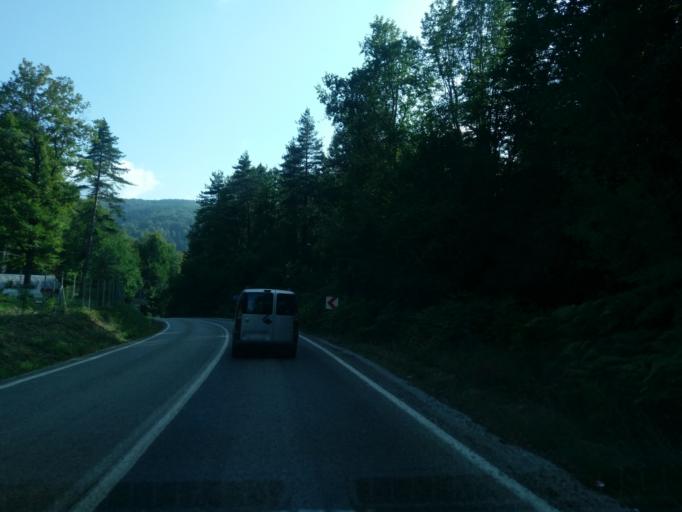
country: TR
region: Sinop
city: Ayancik
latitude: 41.8817
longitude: 34.5138
